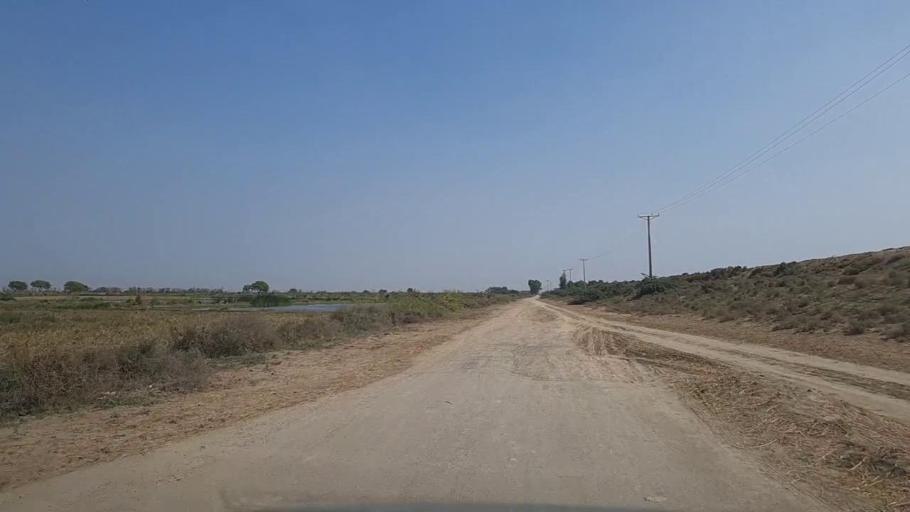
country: PK
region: Sindh
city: Thatta
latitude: 24.5859
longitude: 67.9257
